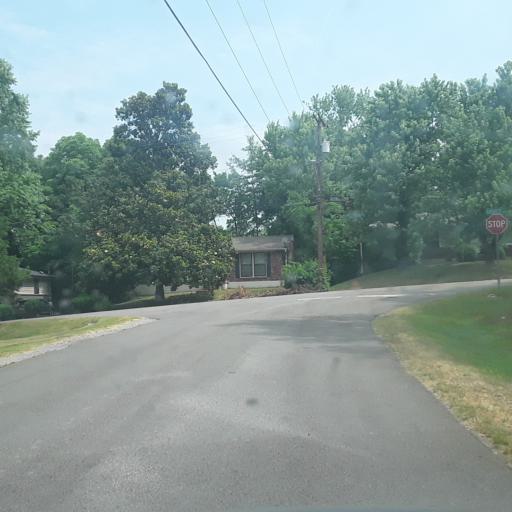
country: US
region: Tennessee
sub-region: Davidson County
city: Oak Hill
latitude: 36.0766
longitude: -86.7433
